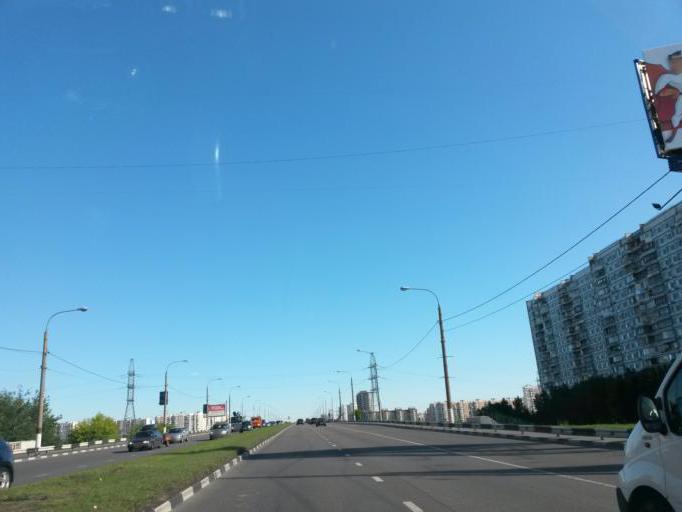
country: RU
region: Moscow
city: Brateyevo
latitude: 55.6357
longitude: 37.7495
